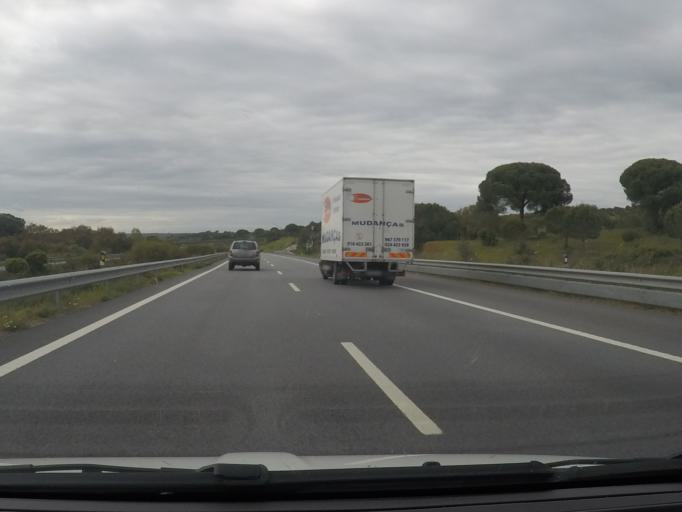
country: PT
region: Setubal
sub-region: Alcacer do Sal
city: Alcacer do Sal
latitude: 38.4795
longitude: -8.5401
